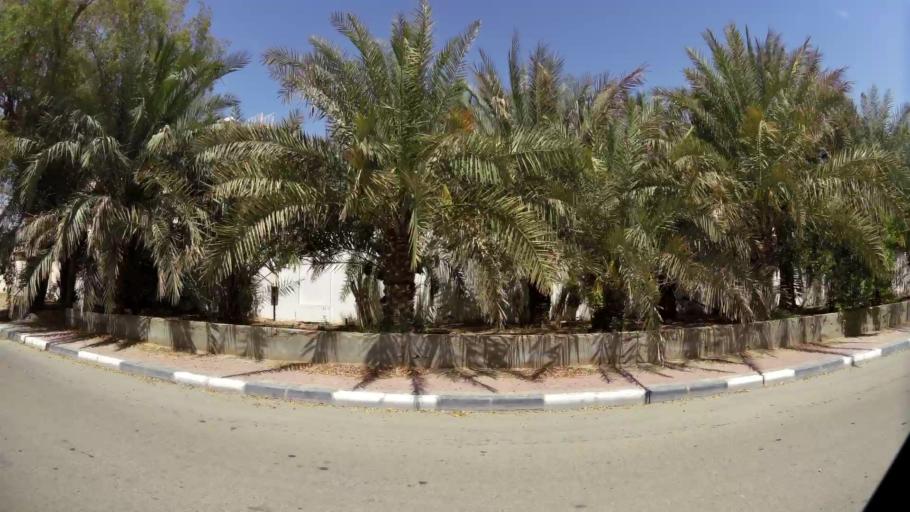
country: OM
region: Al Buraimi
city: Al Buraymi
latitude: 24.2799
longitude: 55.7822
